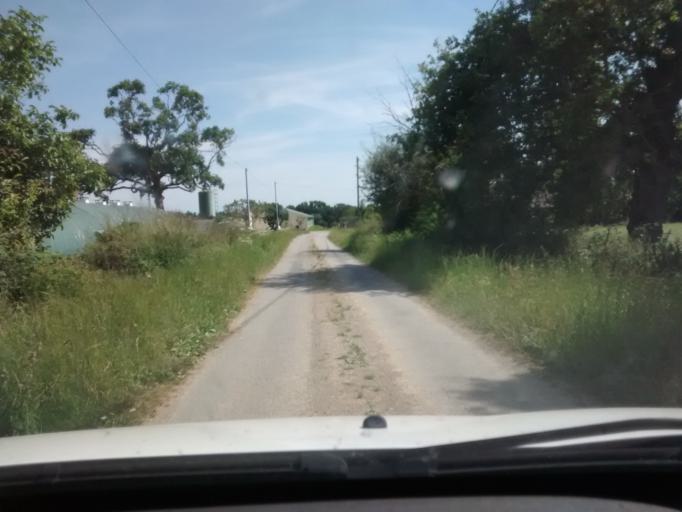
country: FR
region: Brittany
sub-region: Departement d'Ille-et-Vilaine
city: Cesson-Sevigne
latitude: 48.0954
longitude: -1.5704
